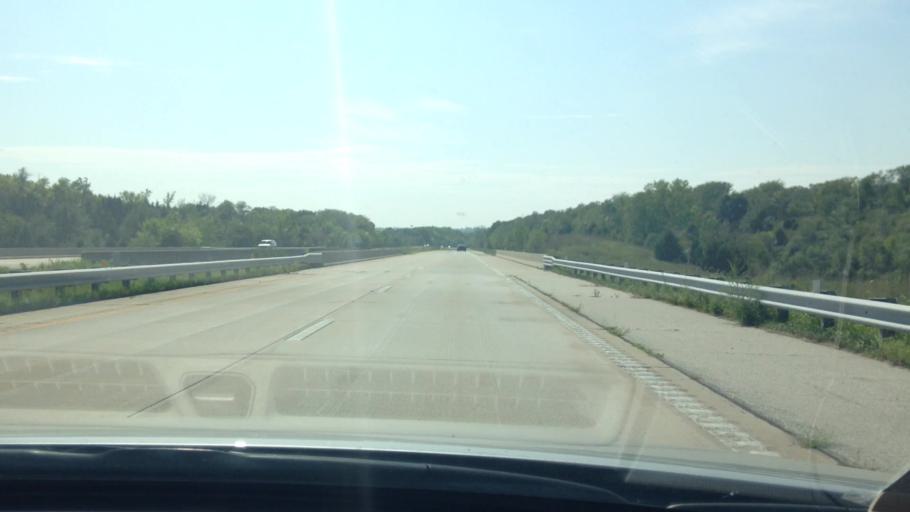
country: US
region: Missouri
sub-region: Platte County
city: Weatherby Lake
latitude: 39.2482
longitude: -94.7329
